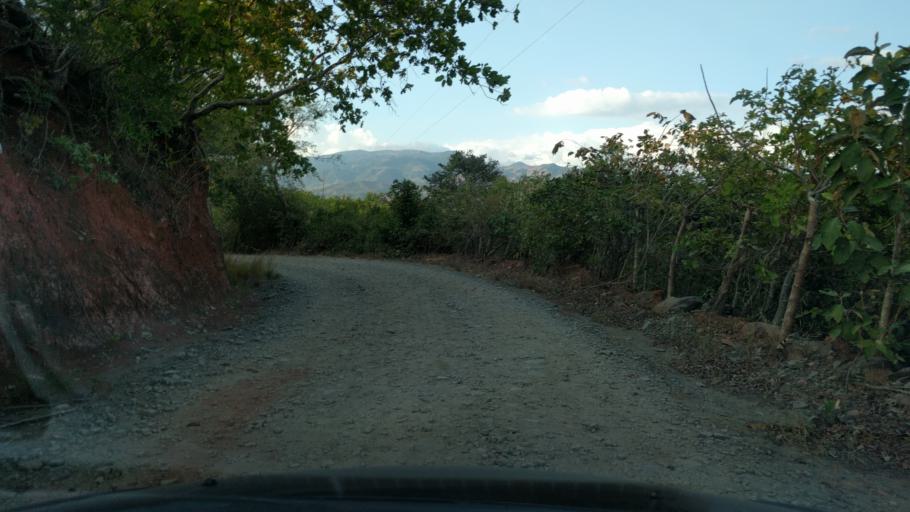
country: CR
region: Puntarenas
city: Esparza
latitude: 10.0245
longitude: -84.6984
